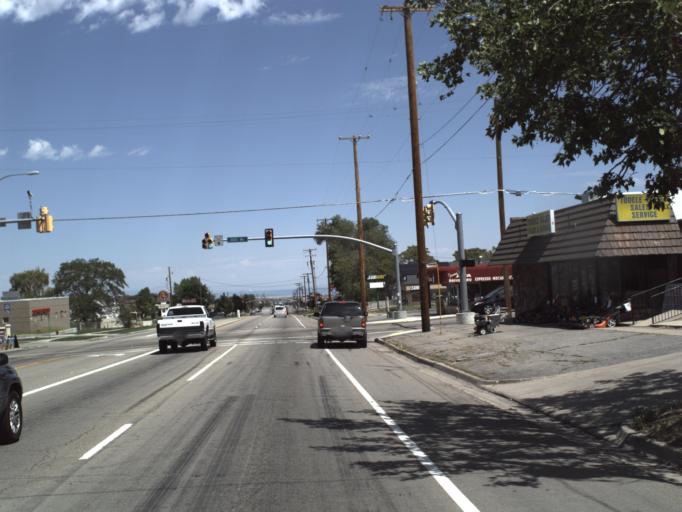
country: US
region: Utah
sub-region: Tooele County
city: Tooele
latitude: 40.5351
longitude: -112.2984
